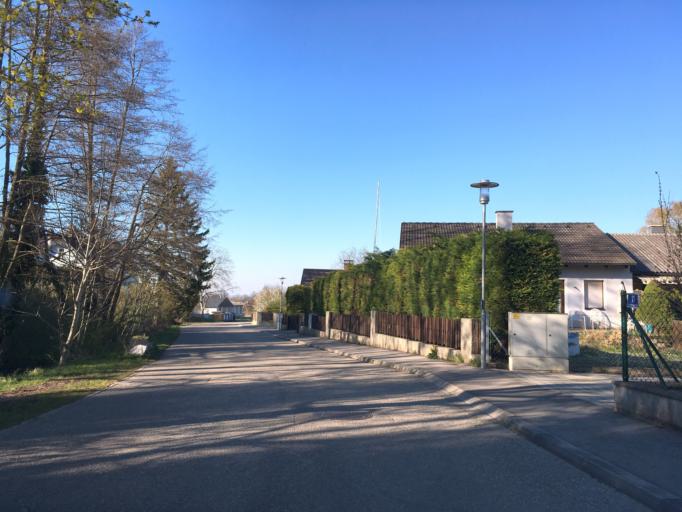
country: AT
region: Lower Austria
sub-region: Politischer Bezirk Tulln
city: Konigstetten
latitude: 48.3001
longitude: 16.1573
